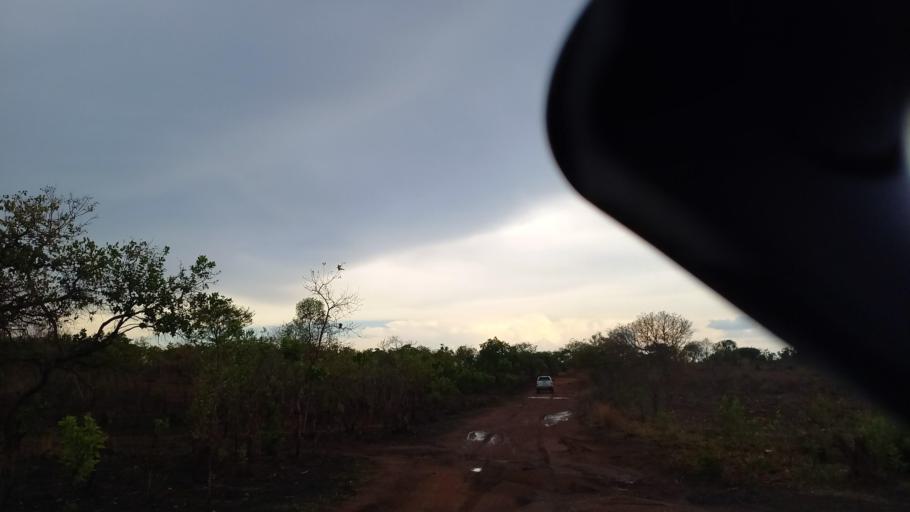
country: ZM
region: Lusaka
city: Kafue
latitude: -16.0234
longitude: 28.2967
